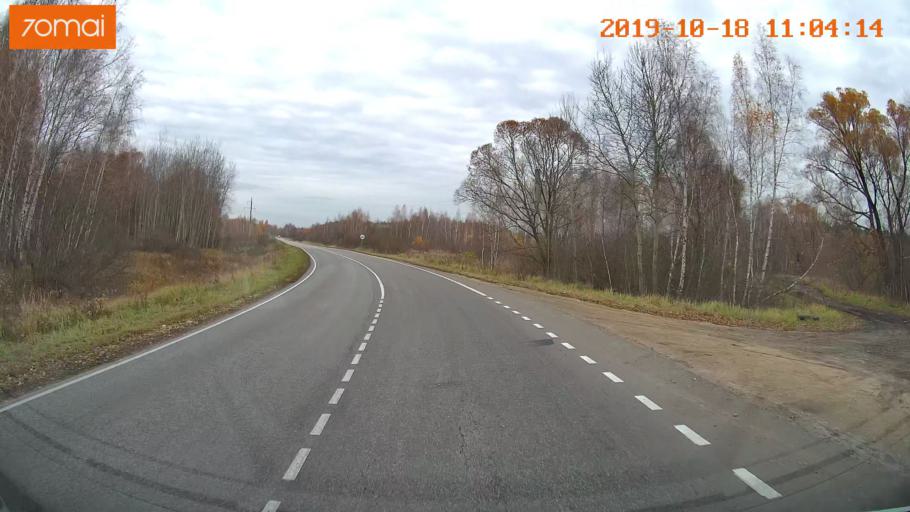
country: RU
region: Tula
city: Yepifan'
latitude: 53.8916
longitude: 38.5504
